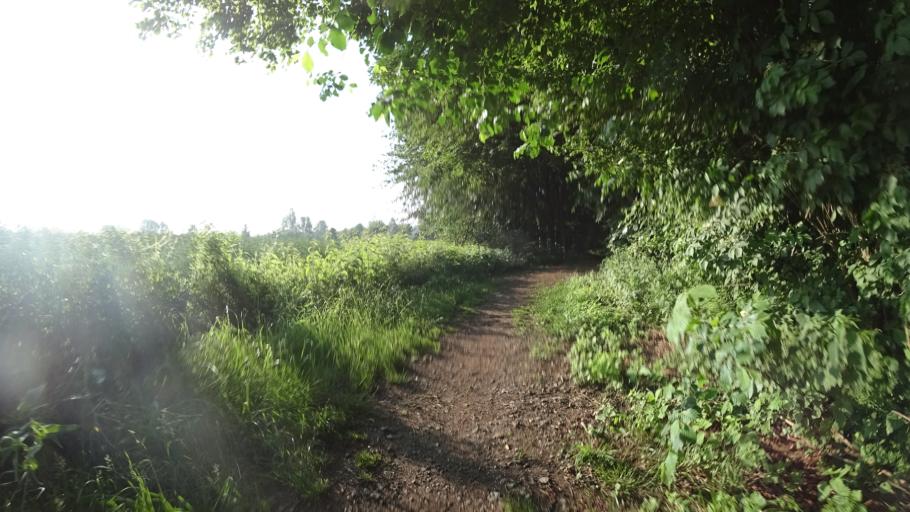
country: DE
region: North Rhine-Westphalia
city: Erwitte
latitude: 51.6336
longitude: 8.3863
